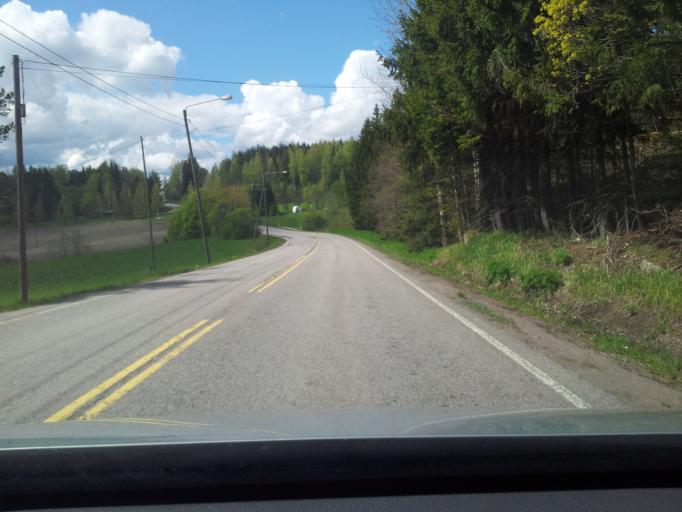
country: FI
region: Uusimaa
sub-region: Loviisa
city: Perna
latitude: 60.4963
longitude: 25.9119
